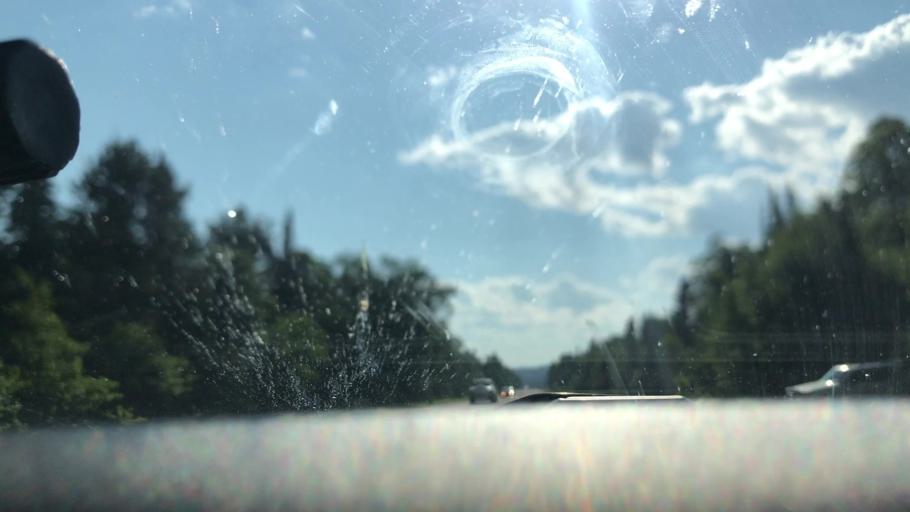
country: US
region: Minnesota
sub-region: Cook County
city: Grand Marais
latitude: 47.7960
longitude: -90.1321
